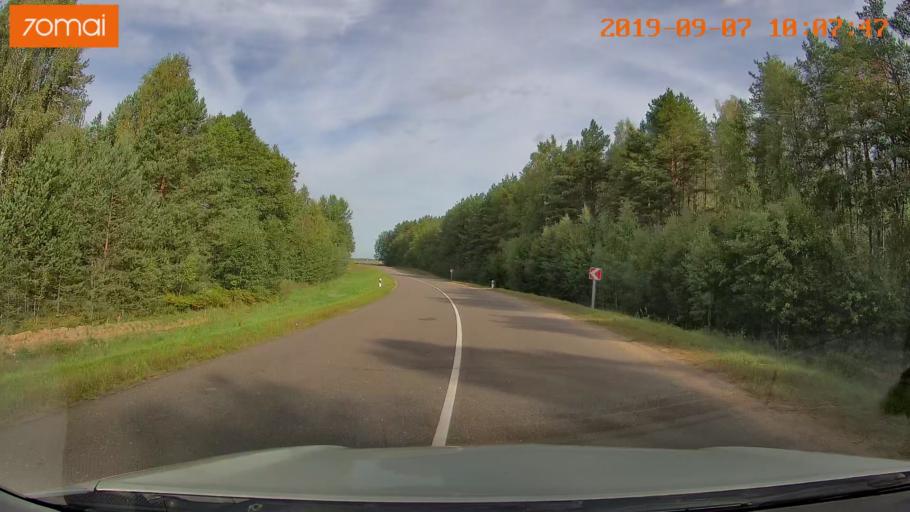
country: BY
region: Grodnenskaya
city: Voranava
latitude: 54.0800
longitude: 25.3954
